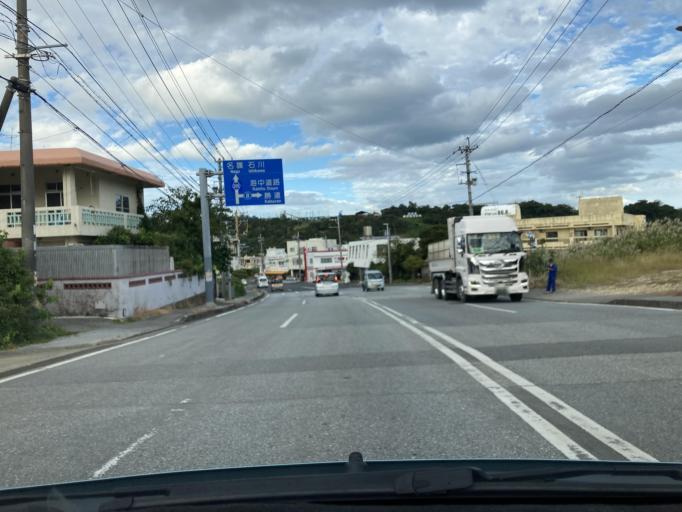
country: JP
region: Okinawa
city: Ishikawa
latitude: 26.3907
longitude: 127.8318
